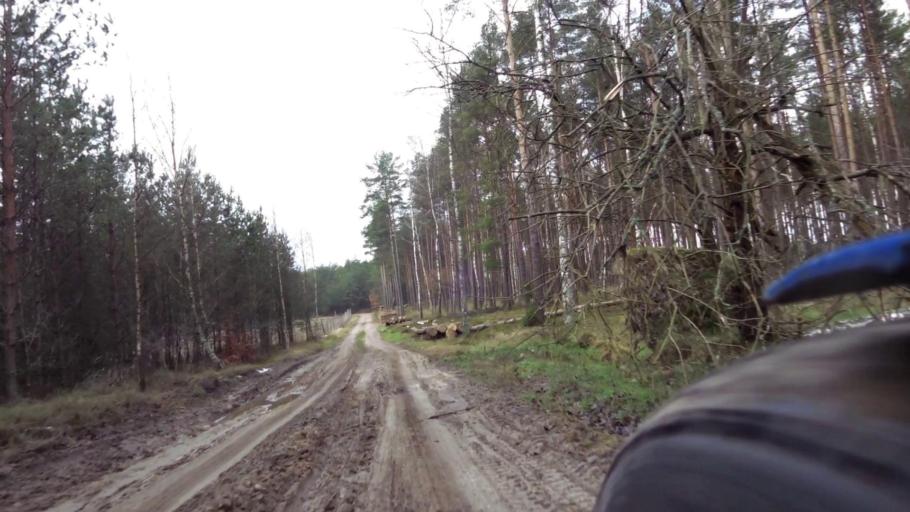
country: PL
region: West Pomeranian Voivodeship
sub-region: Powiat szczecinecki
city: Borne Sulinowo
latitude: 53.6070
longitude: 16.6413
